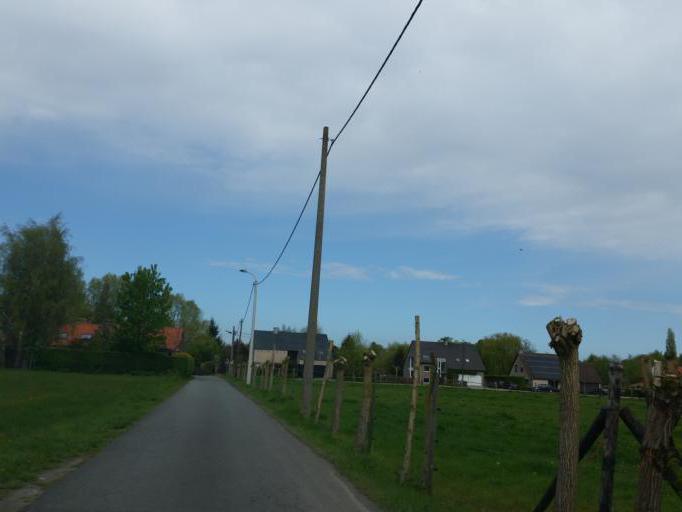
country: BE
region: Flanders
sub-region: Provincie Vlaams-Brabant
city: Boortmeerbeek
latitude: 50.9751
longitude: 4.5528
